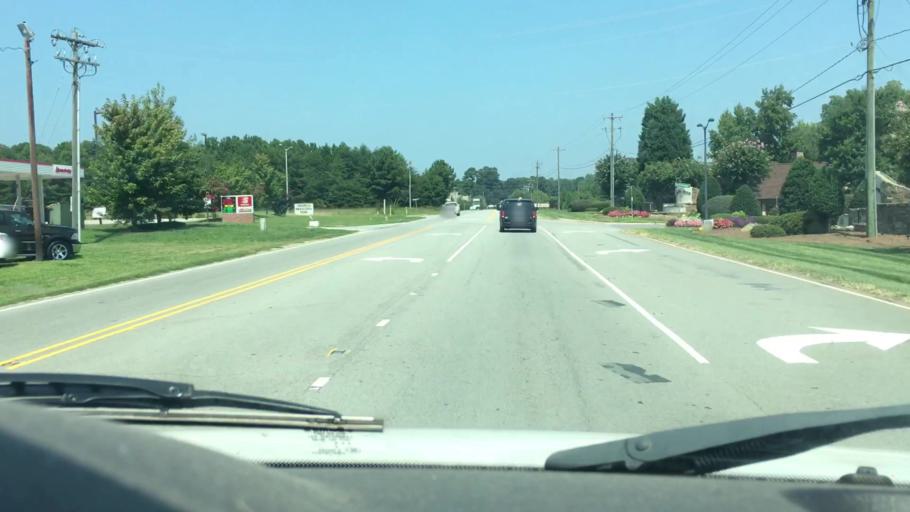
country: US
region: North Carolina
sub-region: Lincoln County
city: Westport
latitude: 35.4837
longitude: -80.9943
